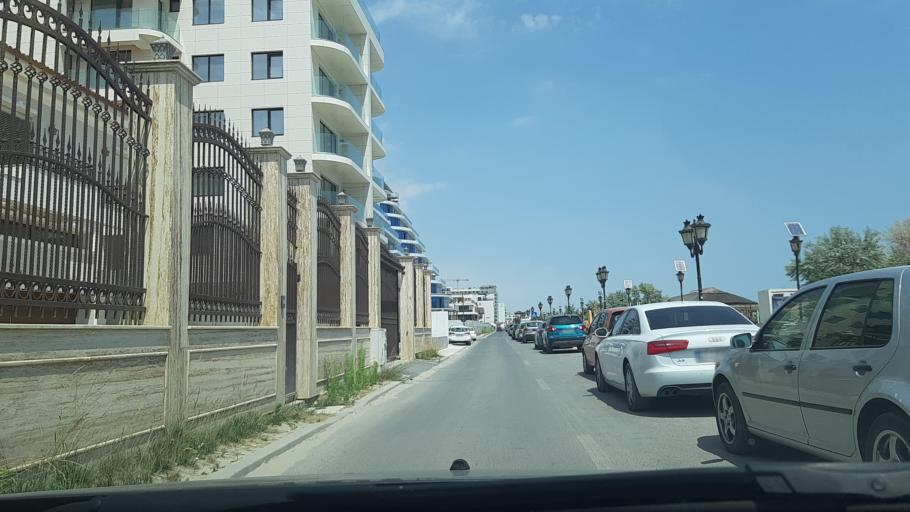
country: RO
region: Constanta
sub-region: Comuna Navodari
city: Navodari
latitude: 44.2882
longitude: 28.6228
